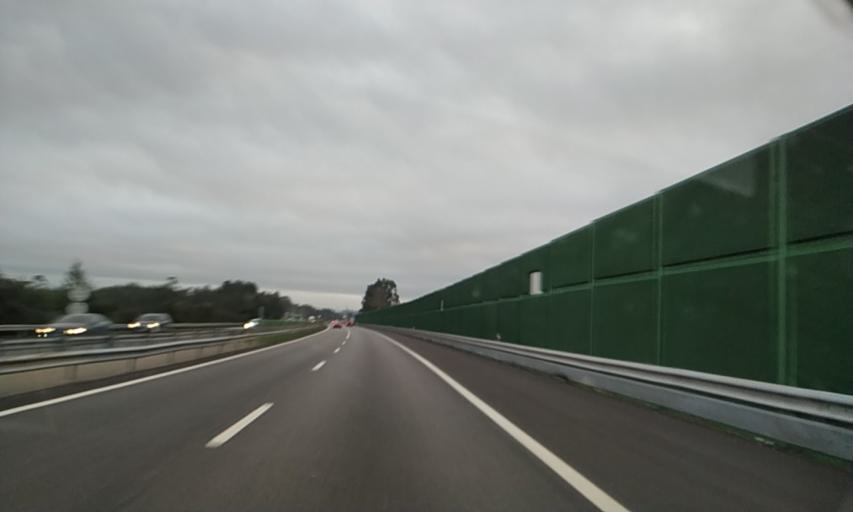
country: PT
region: Aveiro
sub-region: Mealhada
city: Mealhada
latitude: 40.3390
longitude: -8.4951
